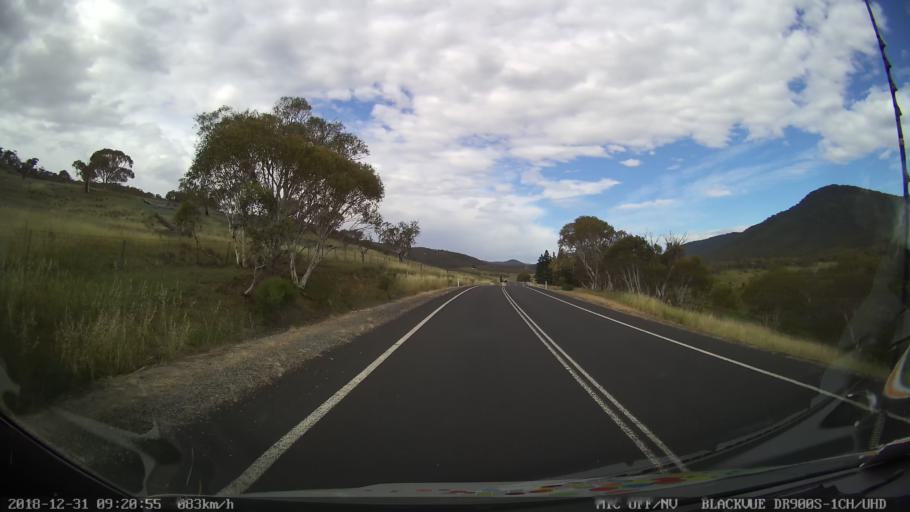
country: AU
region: New South Wales
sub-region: Snowy River
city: Jindabyne
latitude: -36.4249
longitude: 148.5681
